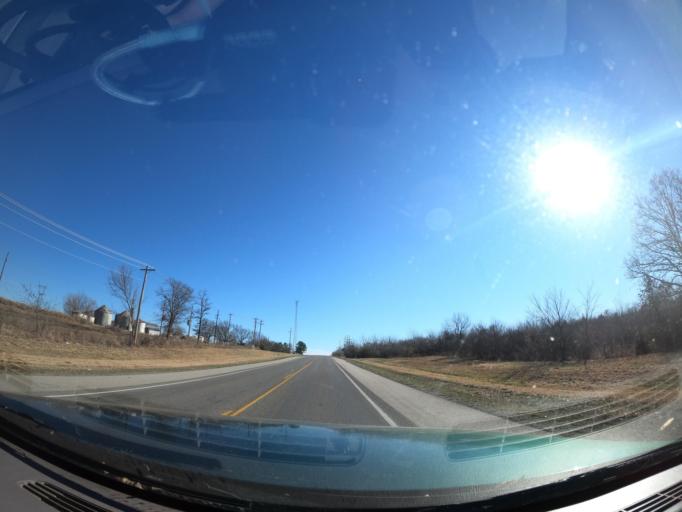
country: US
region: Oklahoma
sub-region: Muskogee County
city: Haskell
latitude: 35.7794
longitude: -95.6605
